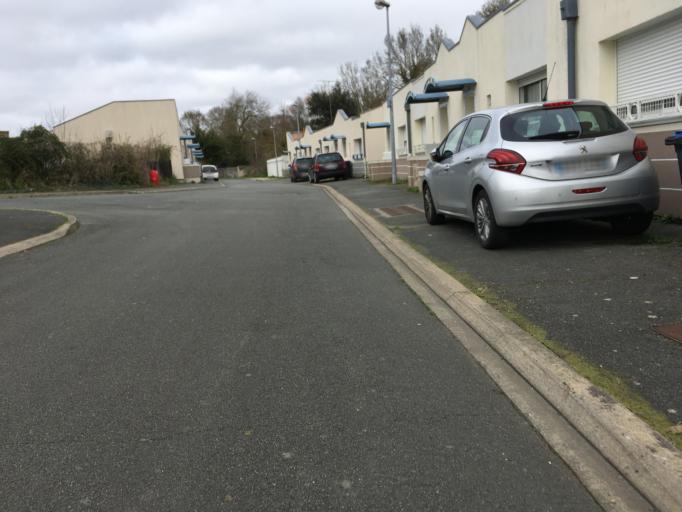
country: FR
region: Poitou-Charentes
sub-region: Departement de la Charente-Maritime
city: La Rochelle
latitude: 46.1762
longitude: -1.1450
